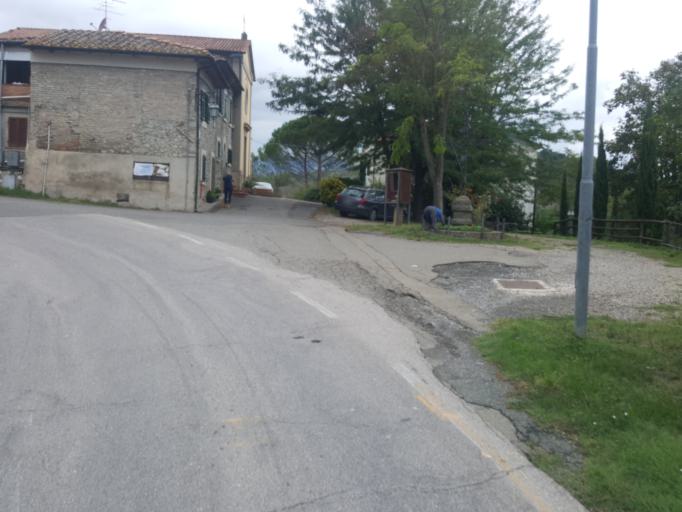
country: IT
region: Tuscany
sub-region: Province of Pisa
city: Saline
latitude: 43.3582
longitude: 10.8134
